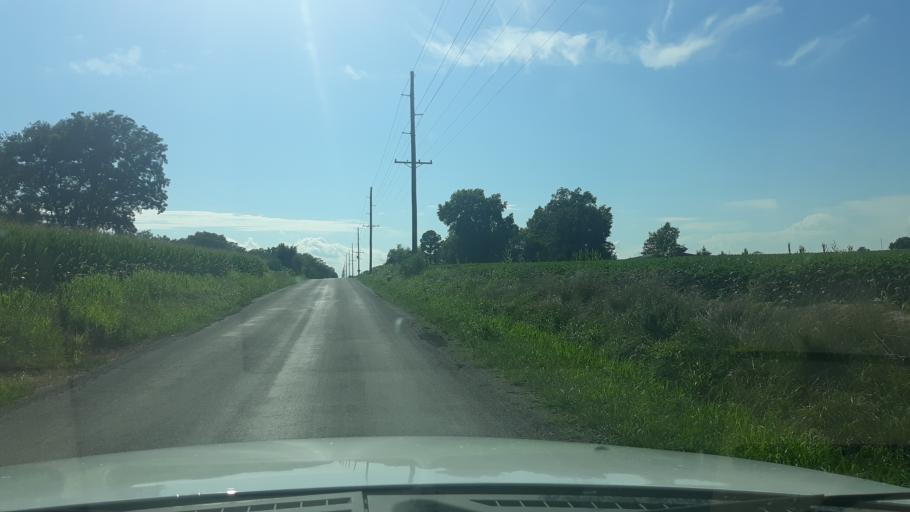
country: US
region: Illinois
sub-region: Saline County
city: Eldorado
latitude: 37.8630
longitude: -88.5451
